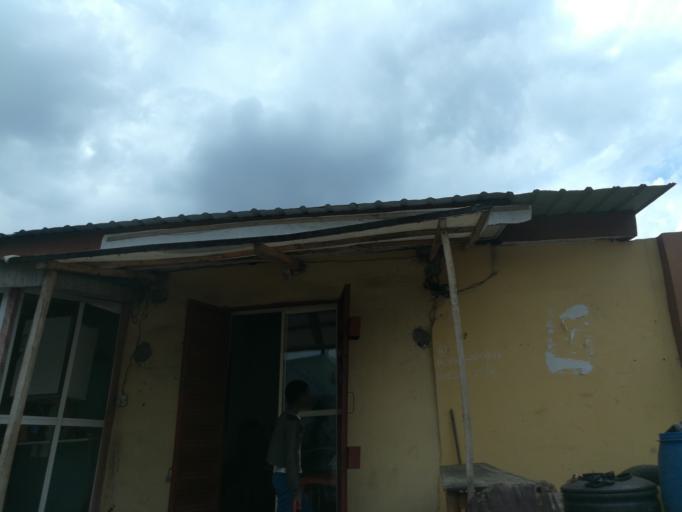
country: NG
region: Lagos
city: Ikeja
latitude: 6.6027
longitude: 3.3491
